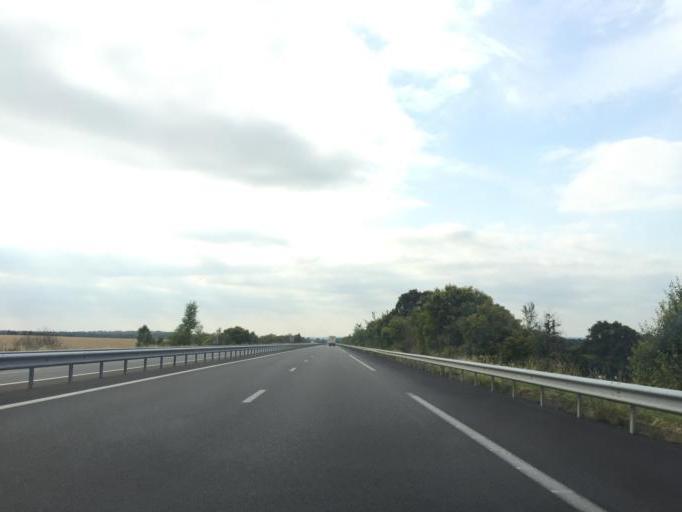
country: FR
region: Auvergne
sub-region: Departement de l'Allier
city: Saint-Francois
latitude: 46.4608
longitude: 3.8908
